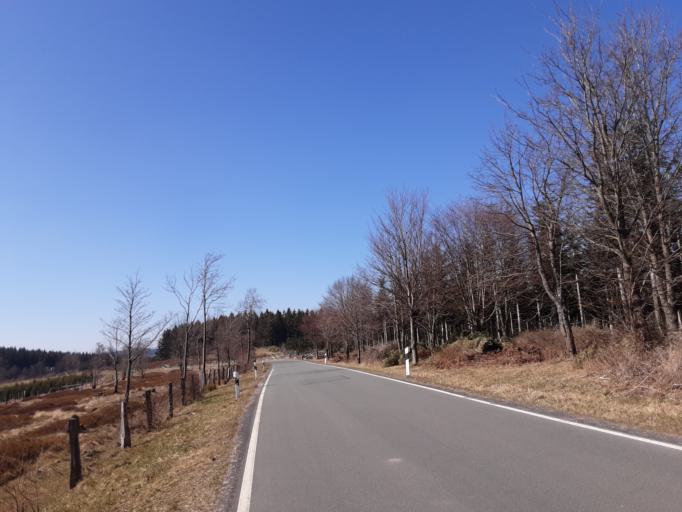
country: DE
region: North Rhine-Westphalia
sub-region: Regierungsbezirk Arnsberg
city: Winterberg
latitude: 51.1971
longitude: 8.4683
